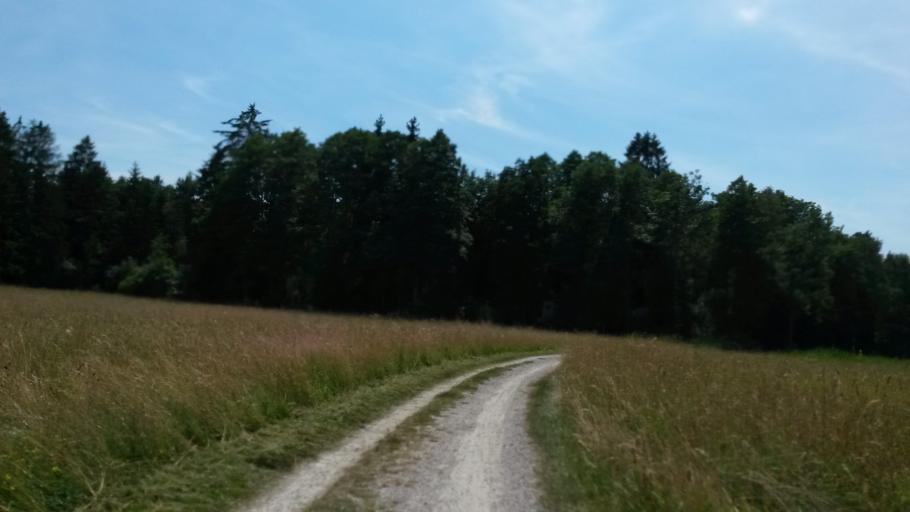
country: DE
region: Bavaria
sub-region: Upper Bavaria
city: Seeon-Seebruck
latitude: 47.9385
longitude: 12.4872
